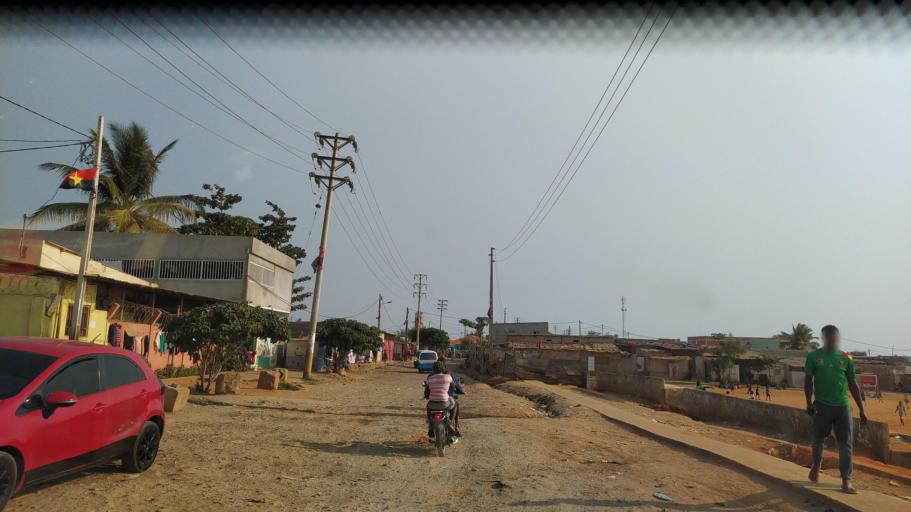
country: AO
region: Luanda
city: Luanda
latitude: -8.8660
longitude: 13.2031
